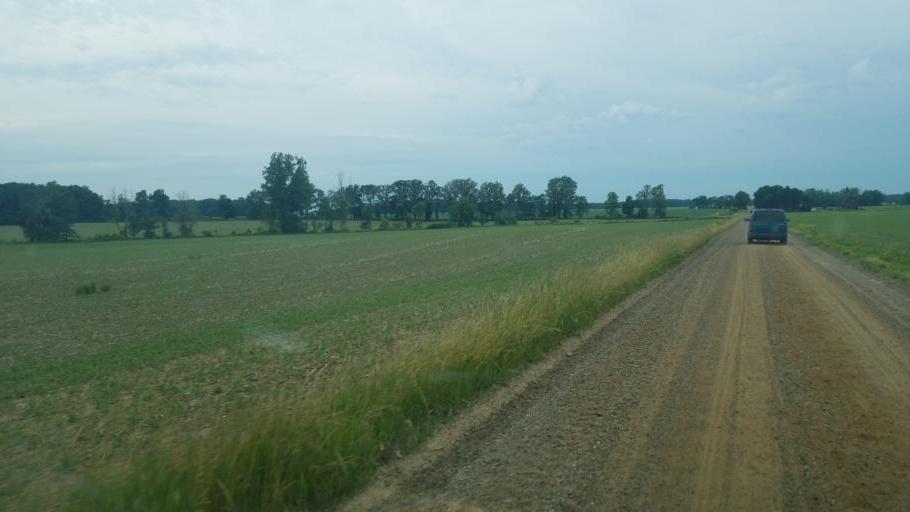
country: US
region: Michigan
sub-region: Barry County
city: Nashville
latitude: 42.6587
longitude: -84.9754
